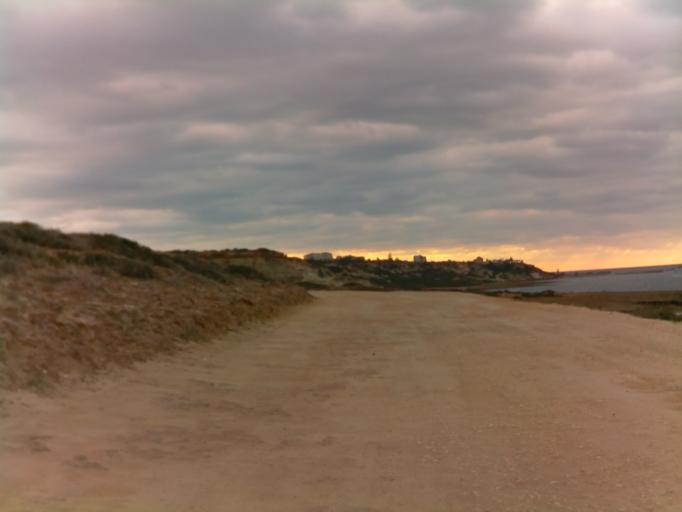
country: CY
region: Pafos
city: Pegeia
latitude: 34.9163
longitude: 32.3272
